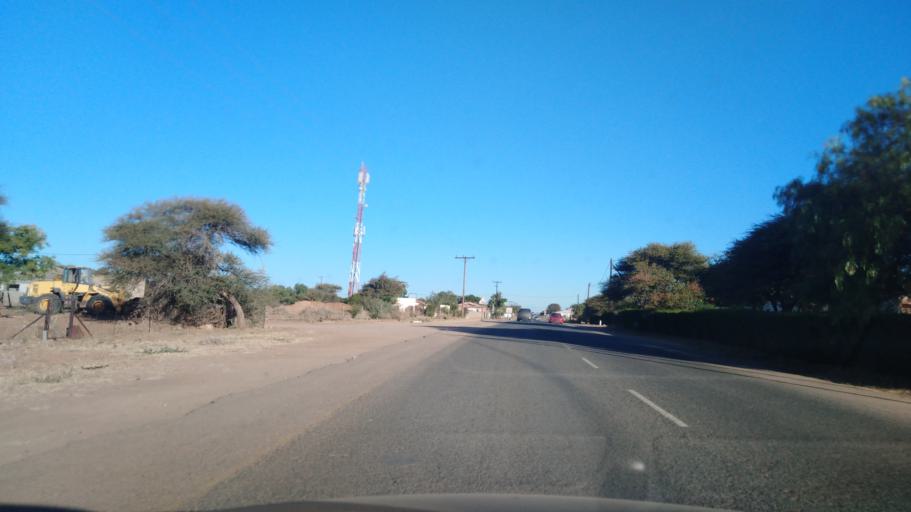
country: BW
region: Central
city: Mahalapye
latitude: -23.0813
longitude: 26.8226
